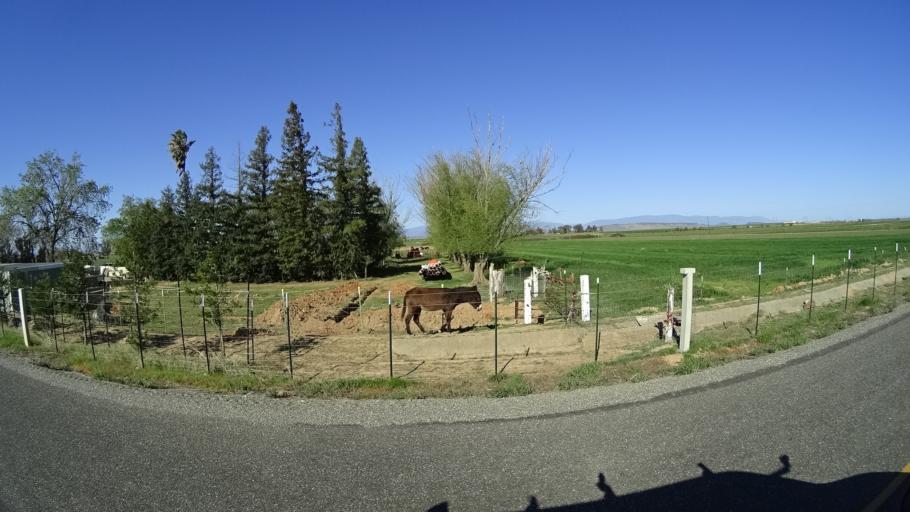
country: US
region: California
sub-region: Glenn County
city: Orland
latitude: 39.7412
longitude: -122.2481
